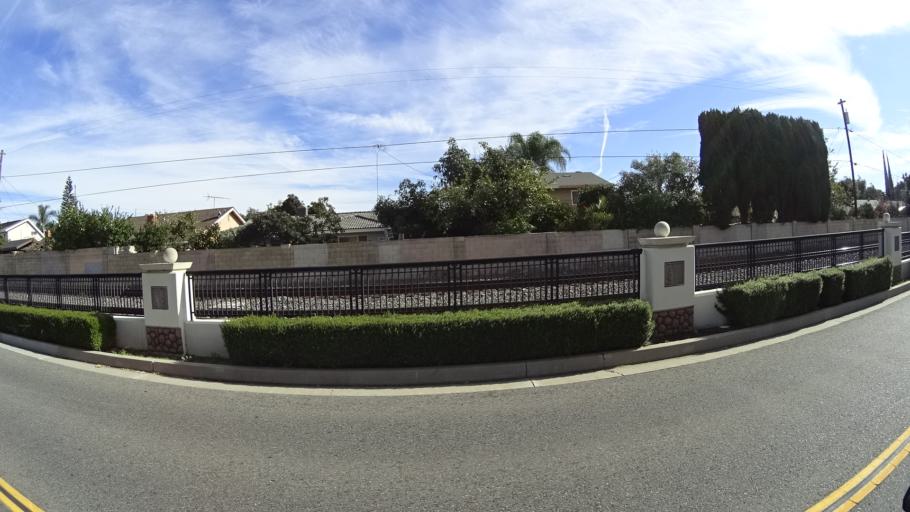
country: US
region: California
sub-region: Orange County
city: Santa Ana
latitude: 33.7649
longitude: -117.8561
